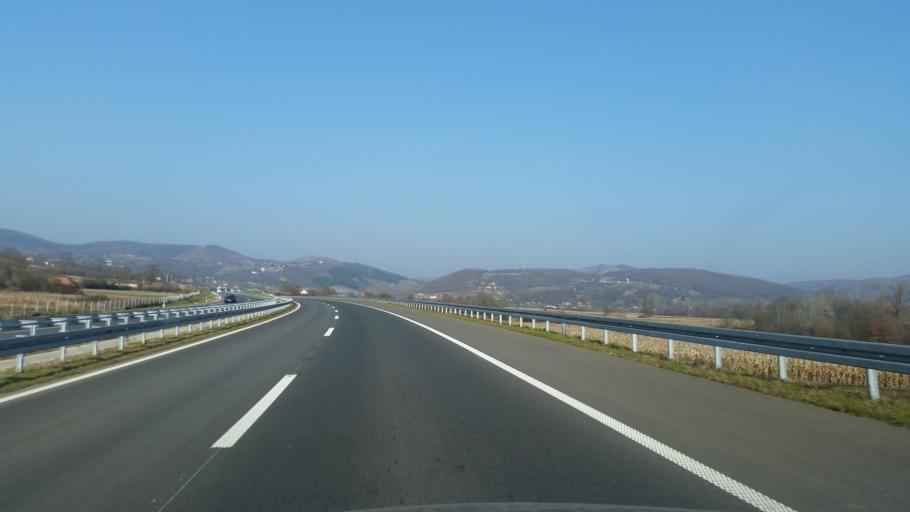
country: RS
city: Prislonica
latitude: 43.9514
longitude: 20.4009
